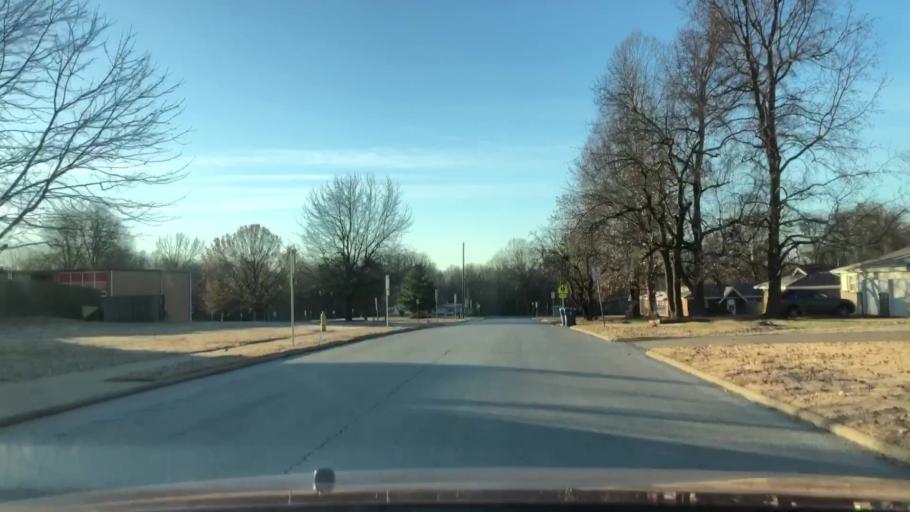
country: US
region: Missouri
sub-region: Greene County
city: Springfield
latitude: 37.1751
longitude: -93.2434
